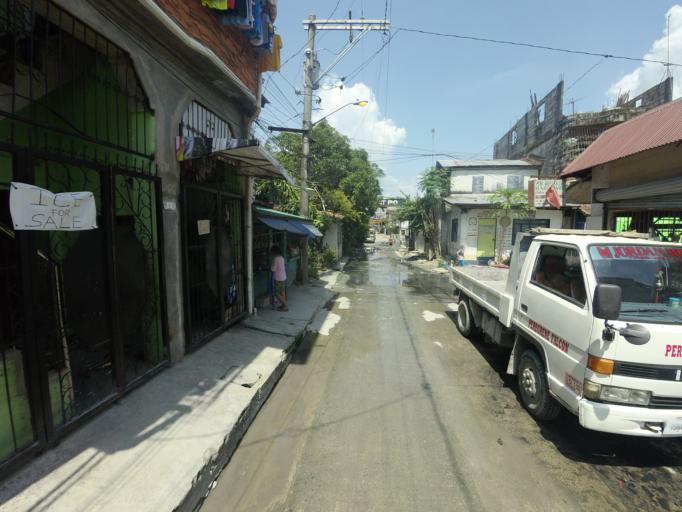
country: PH
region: Calabarzon
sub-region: Province of Rizal
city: Taytay
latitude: 14.5423
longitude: 121.1063
